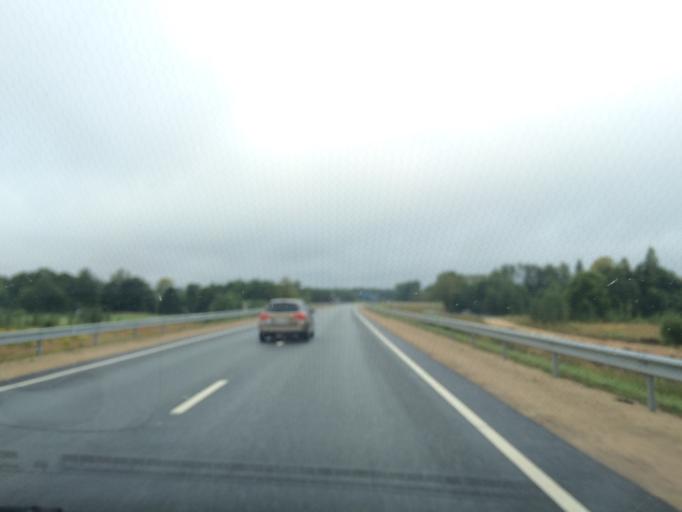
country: LV
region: Kegums
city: Kegums
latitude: 56.8228
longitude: 24.7679
